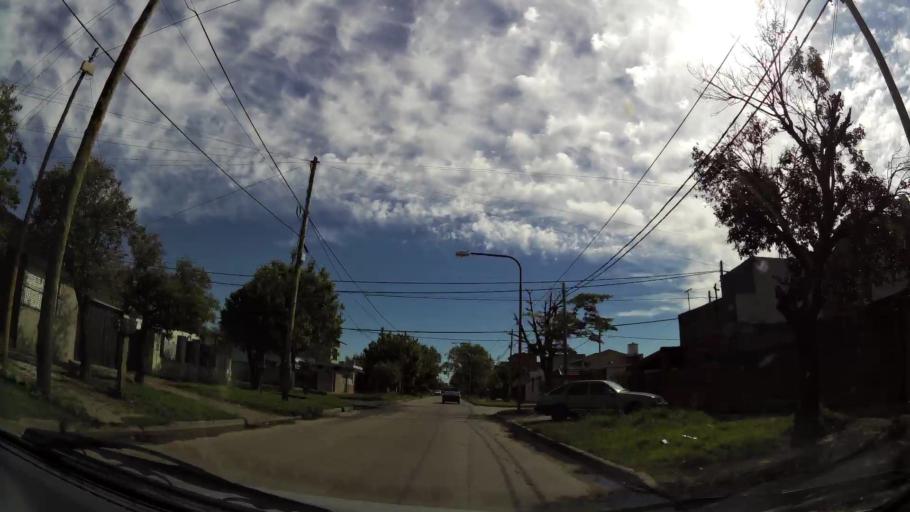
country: AR
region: Buenos Aires
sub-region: Partido de Quilmes
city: Quilmes
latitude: -34.7738
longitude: -58.2914
